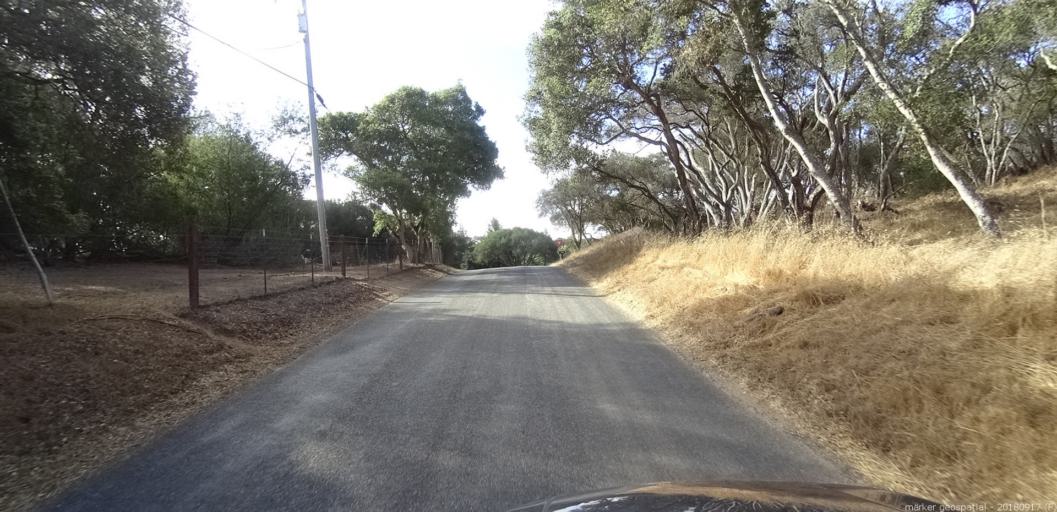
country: US
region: California
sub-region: Monterey County
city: Elkhorn
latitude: 36.8082
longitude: -121.7135
